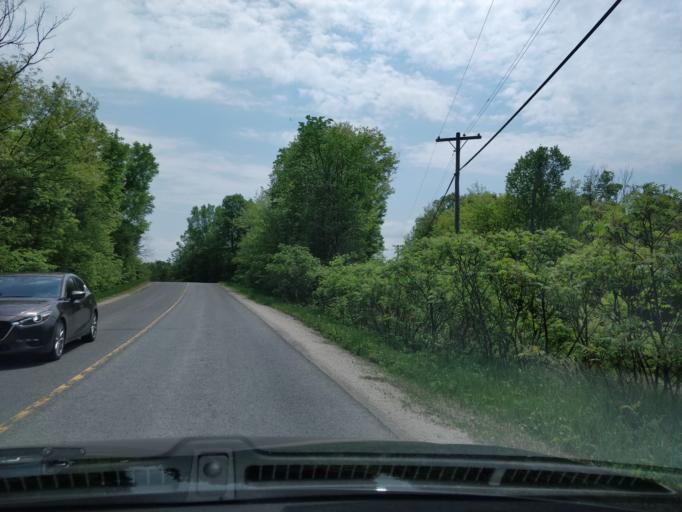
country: CA
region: Ontario
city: Perth
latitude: 44.6489
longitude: -76.5392
